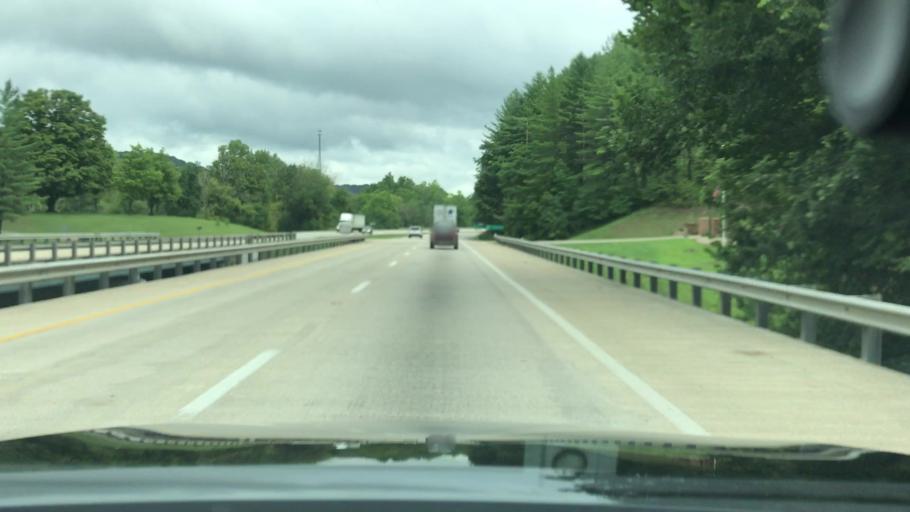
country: US
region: Ohio
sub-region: Jackson County
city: Jackson
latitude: 39.1906
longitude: -82.7698
